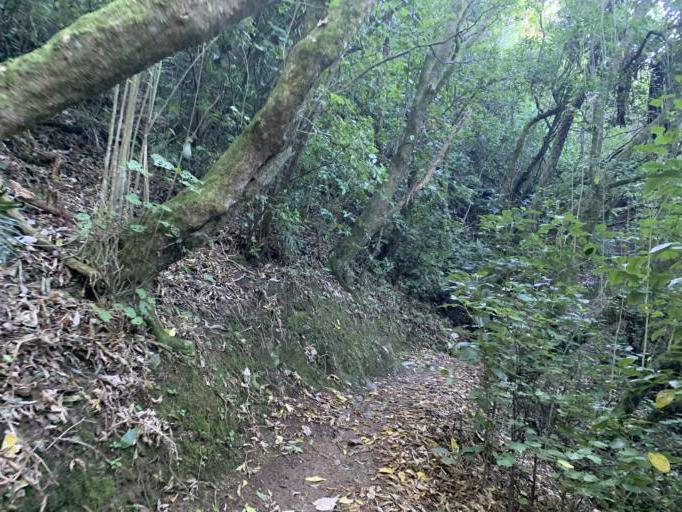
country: NZ
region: Wellington
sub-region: Wellington City
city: Brooklyn
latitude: -41.2981
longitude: 174.7542
